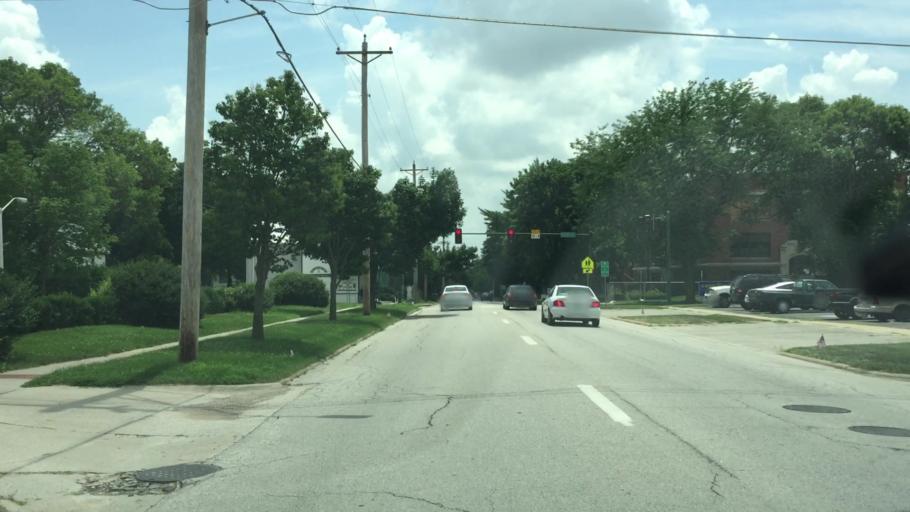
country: US
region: Iowa
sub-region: Johnson County
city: Iowa City
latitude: 41.6685
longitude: -91.5257
